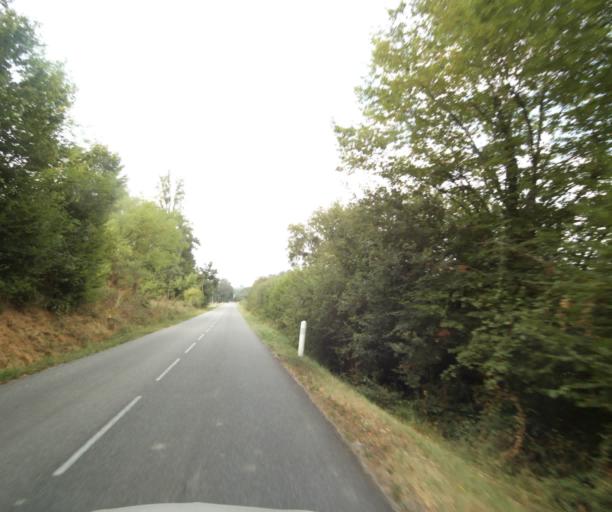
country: FR
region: Aquitaine
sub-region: Departement de la Gironde
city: Creon
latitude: 44.7628
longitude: -0.3623
